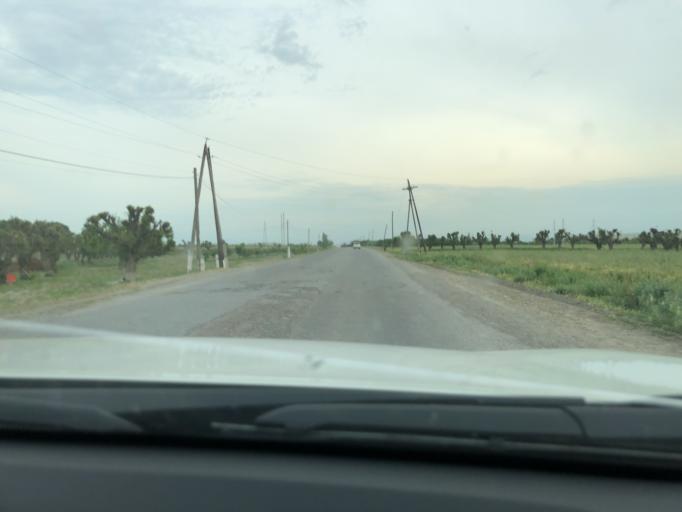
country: UZ
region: Toshkent
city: Bekobod
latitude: 40.1554
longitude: 69.2542
